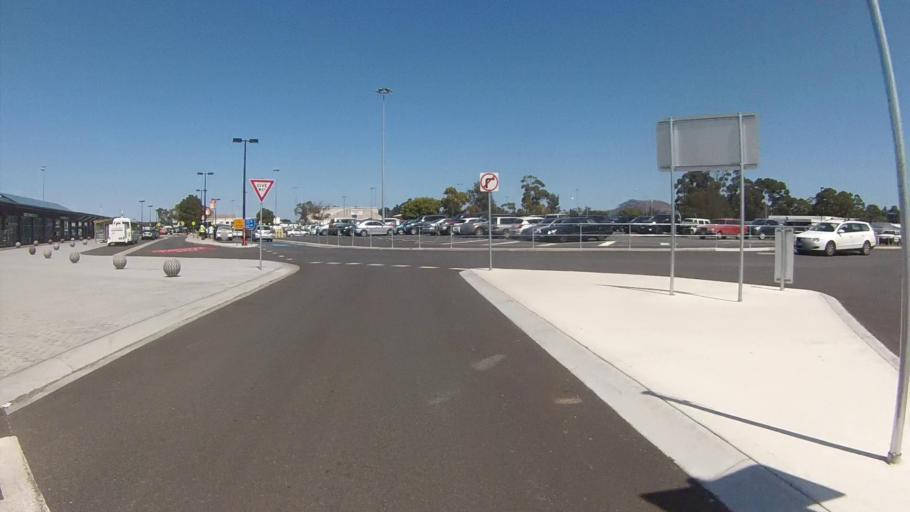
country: AU
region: Tasmania
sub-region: Clarence
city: Seven Mile Beach
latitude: -42.8364
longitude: 147.5038
